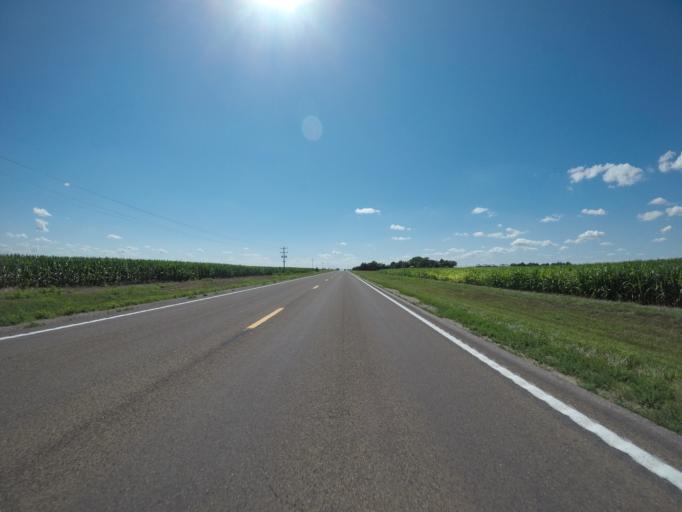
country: US
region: Nebraska
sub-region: Chase County
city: Imperial
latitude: 40.5375
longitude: -101.8035
